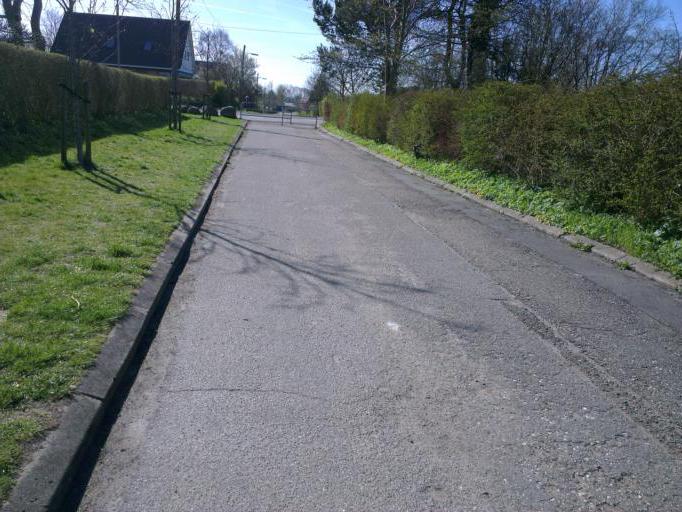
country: DK
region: Capital Region
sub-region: Frederikssund Kommune
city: Frederikssund
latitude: 55.8234
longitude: 12.0803
